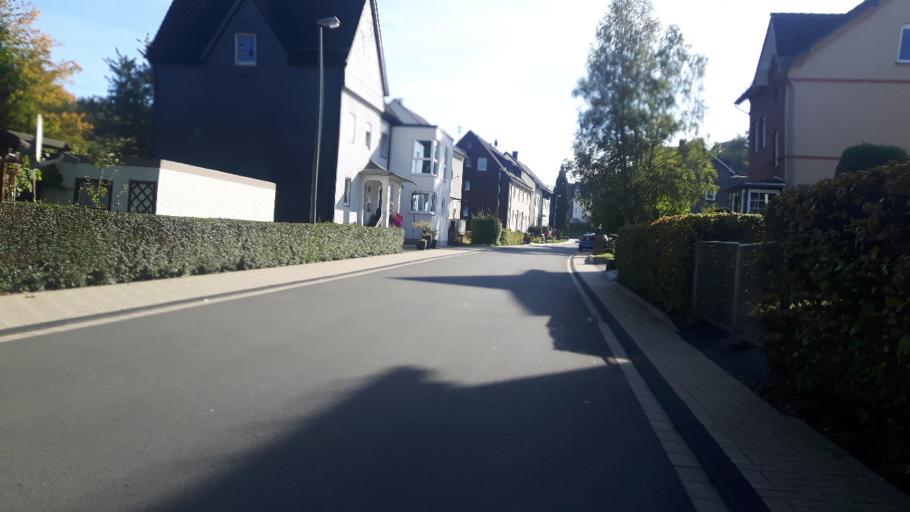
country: DE
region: North Rhine-Westphalia
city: Netphen
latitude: 50.9120
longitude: 8.0537
